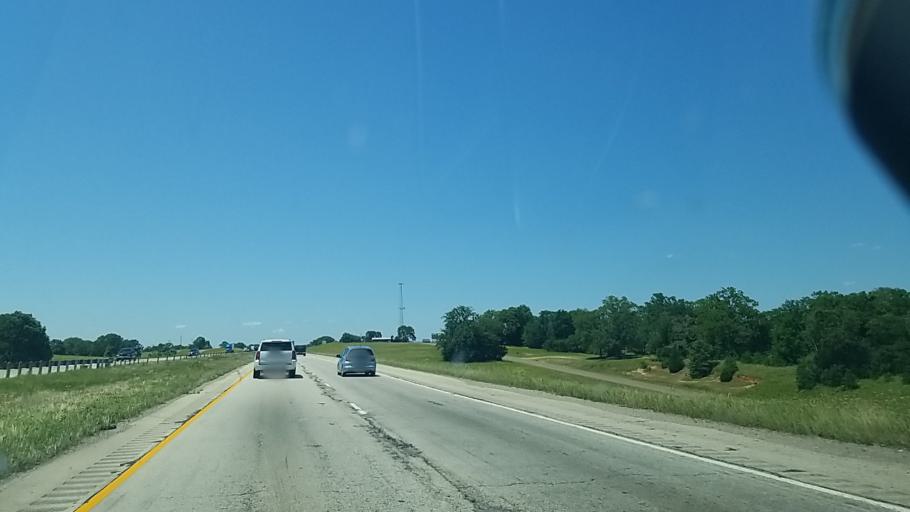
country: US
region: Texas
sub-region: Leon County
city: Buffalo
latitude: 31.4117
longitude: -96.0424
